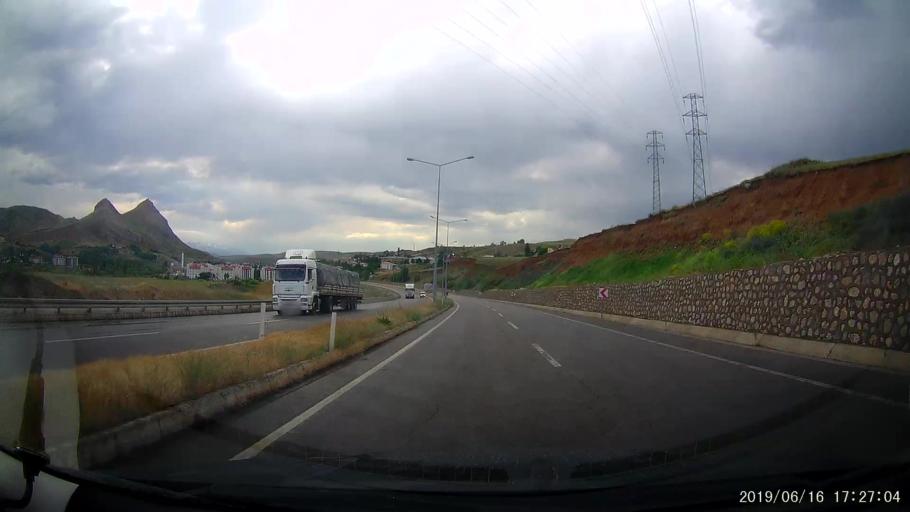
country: TR
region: Erzincan
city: Tercan
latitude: 39.7744
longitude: 40.4001
